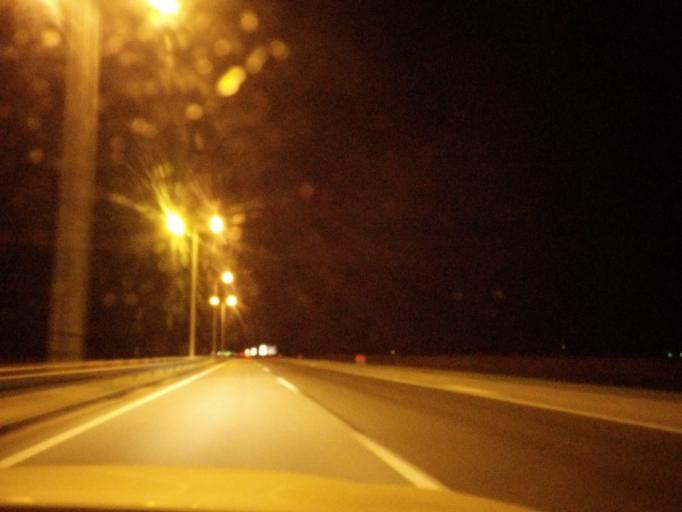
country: RS
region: Autonomna Pokrajina Vojvodina
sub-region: Sremski Okrug
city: Pecinci
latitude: 44.9260
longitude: 19.9444
